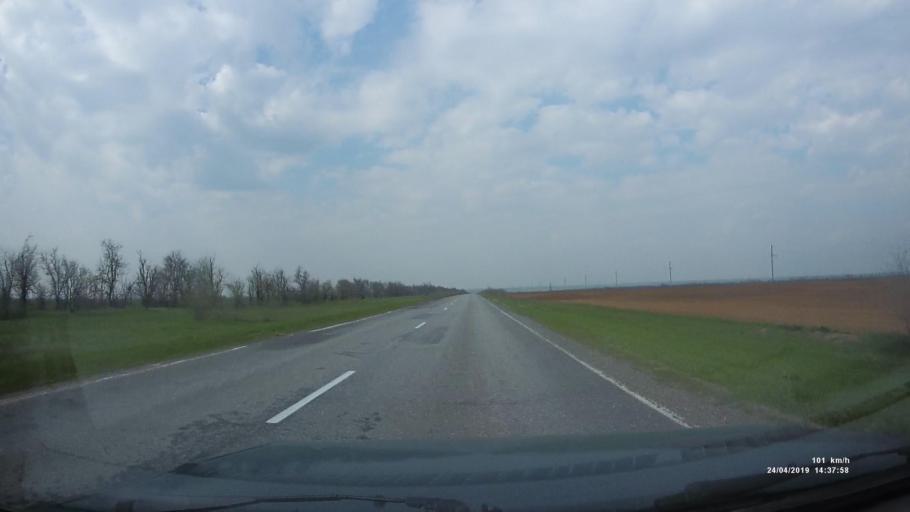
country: RU
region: Rostov
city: Remontnoye
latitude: 46.3939
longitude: 43.8862
